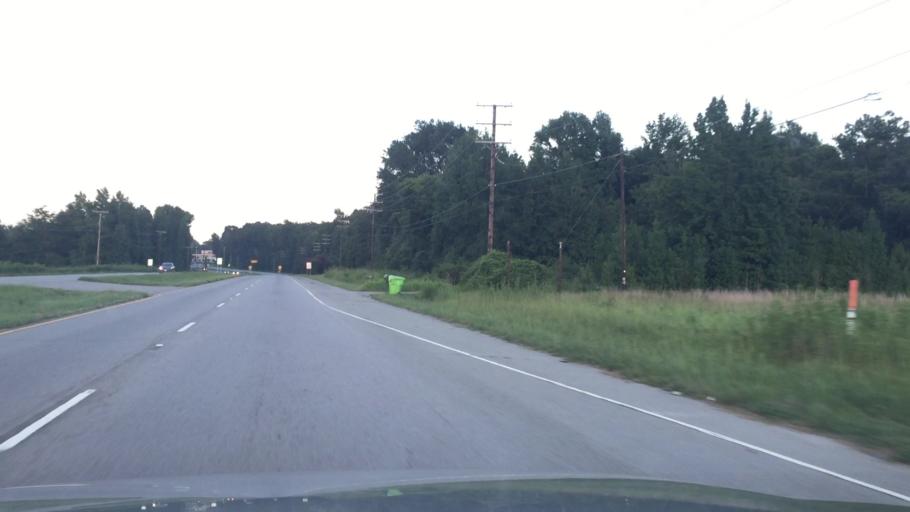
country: US
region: South Carolina
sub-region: Richland County
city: Hopkins
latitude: 33.9444
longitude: -80.8806
